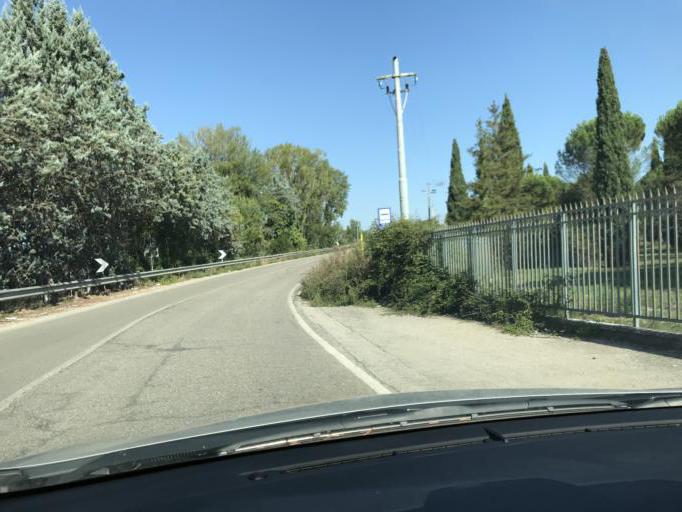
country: IT
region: Umbria
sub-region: Provincia di Perugia
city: Via Lippia
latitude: 43.1066
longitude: 12.4753
